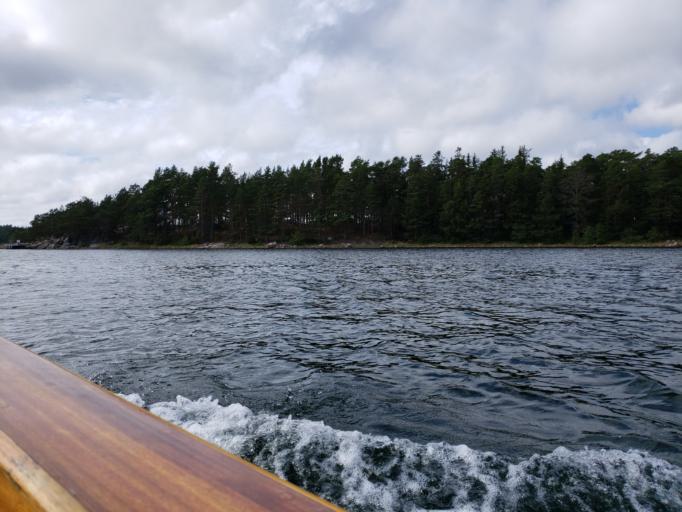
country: FI
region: Varsinais-Suomi
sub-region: Aboland-Turunmaa
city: Dragsfjaerd
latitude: 59.9167
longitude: 22.3952
